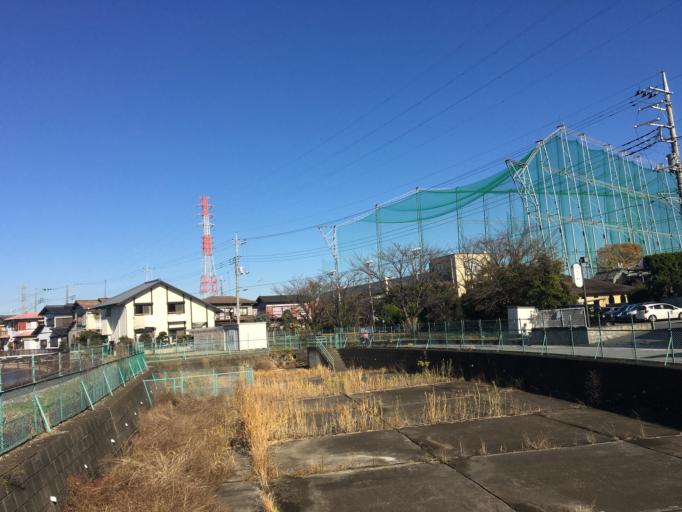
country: JP
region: Saitama
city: Satte
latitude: 36.0686
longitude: 139.7087
